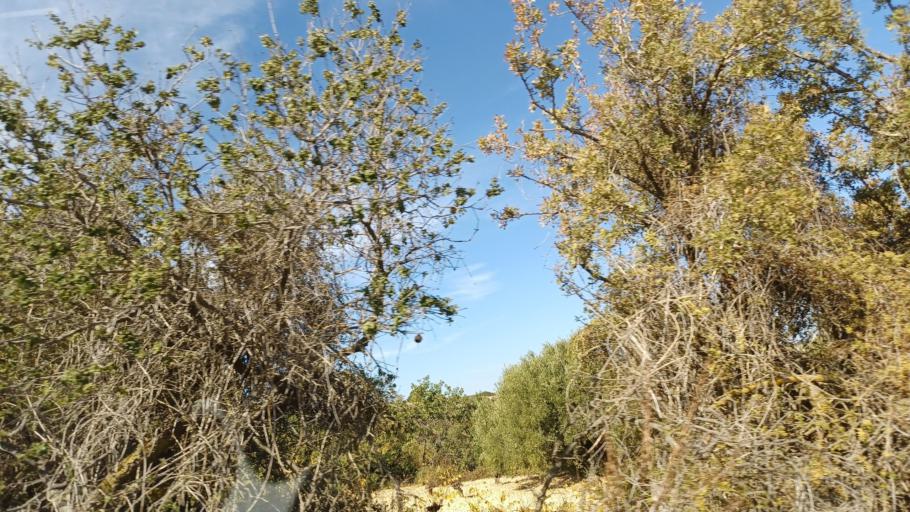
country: CY
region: Pafos
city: Pegeia
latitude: 34.9329
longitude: 32.4503
